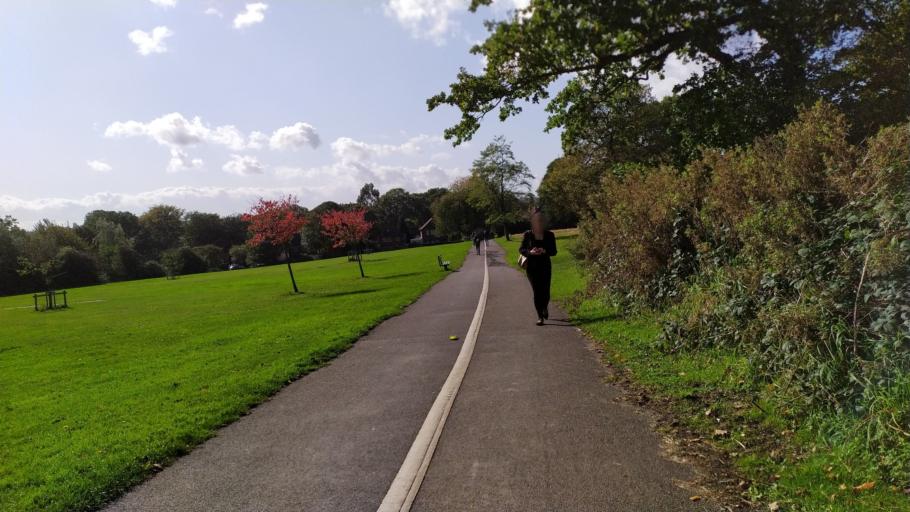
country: GB
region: England
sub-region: City and Borough of Leeds
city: Horsforth
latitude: 53.8240
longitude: -1.5939
